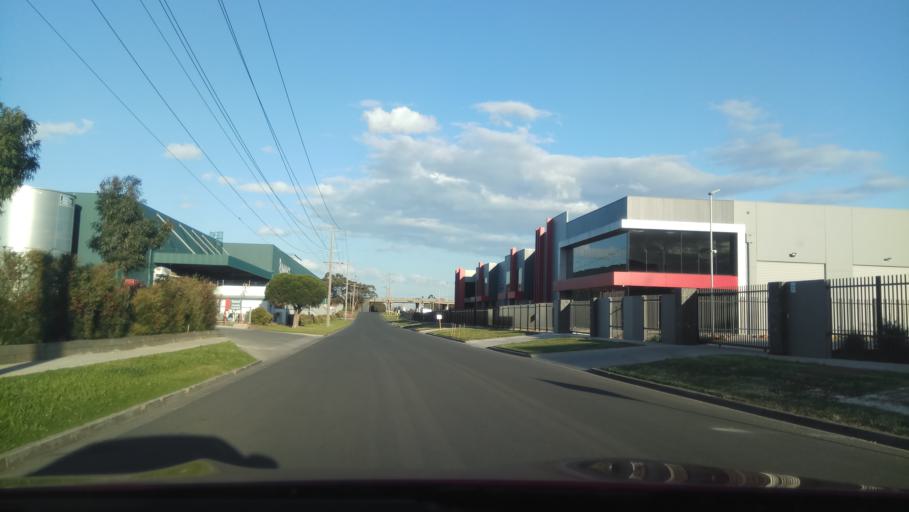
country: AU
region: Victoria
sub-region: Hobsons Bay
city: Altona North
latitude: -37.8458
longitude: 144.8416
